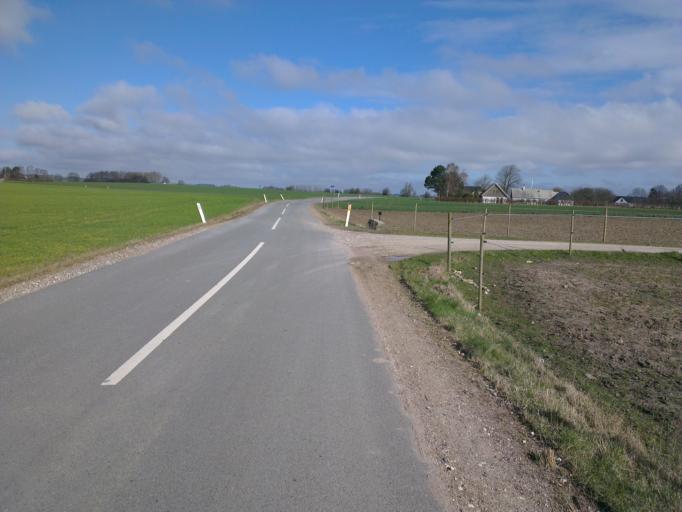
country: DK
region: Capital Region
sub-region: Hillerod Kommune
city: Skaevinge
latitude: 55.8689
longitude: 12.1151
